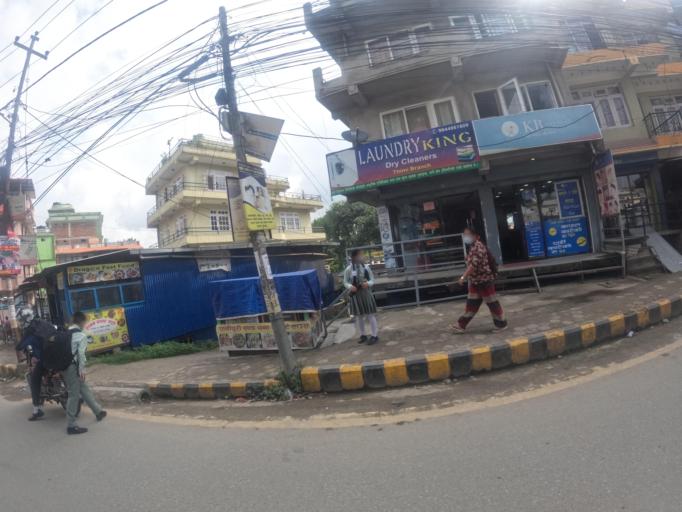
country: NP
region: Central Region
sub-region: Bagmati Zone
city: Bhaktapur
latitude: 27.6686
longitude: 85.3859
